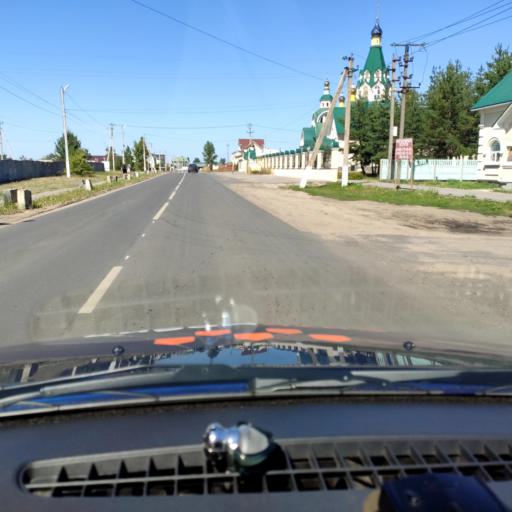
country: RU
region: Voronezj
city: Podgornoye
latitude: 51.7874
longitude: 39.1461
